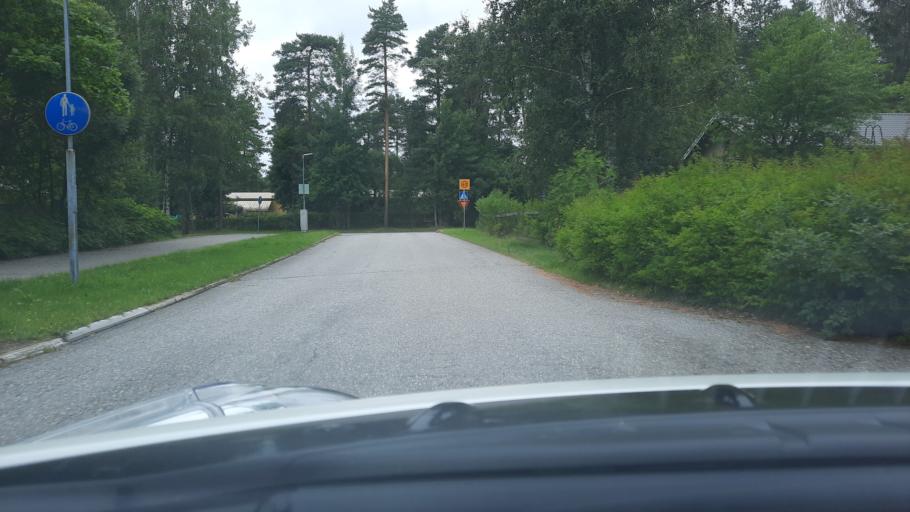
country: FI
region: North Karelia
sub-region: Joensuu
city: Joensuu
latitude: 62.6131
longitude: 29.8333
